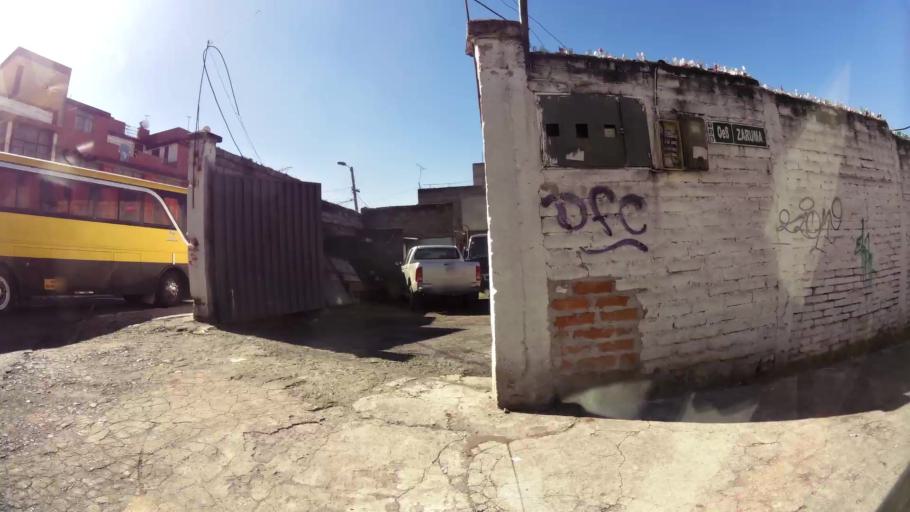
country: EC
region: Pichincha
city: Quito
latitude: -0.2382
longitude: -78.5326
